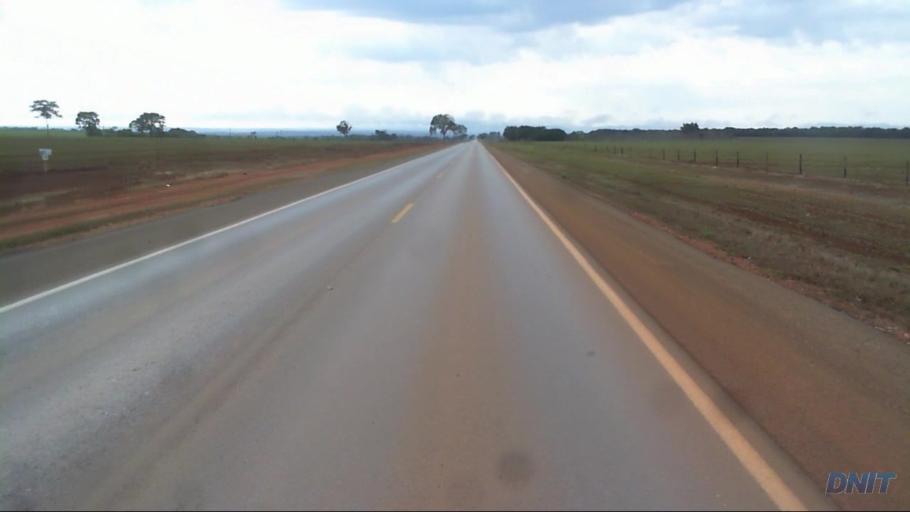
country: BR
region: Goias
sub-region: Uruacu
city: Uruacu
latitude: -14.6971
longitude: -49.1215
